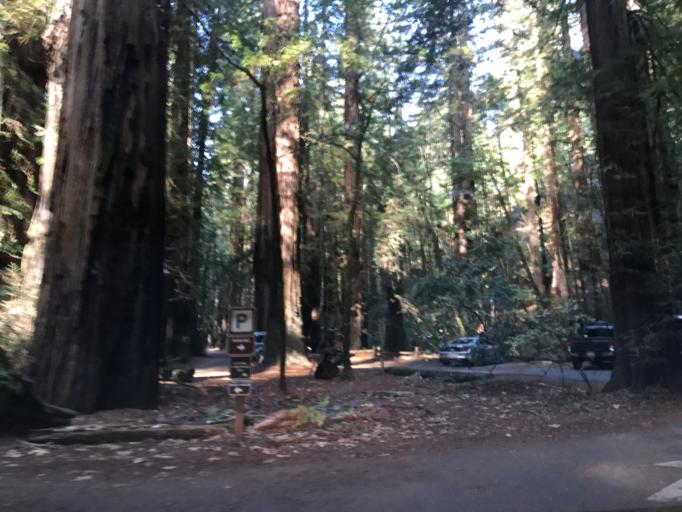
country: US
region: California
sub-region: Sonoma County
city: Guerneville
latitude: 38.5372
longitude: -123.0075
